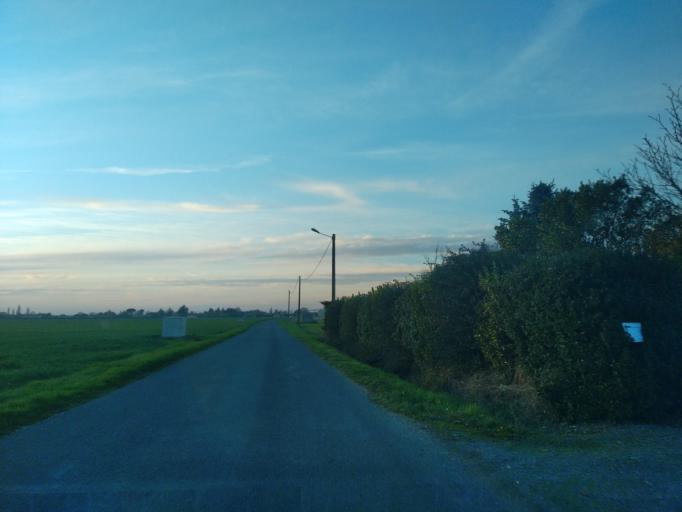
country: FR
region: Pays de la Loire
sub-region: Departement de la Vendee
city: Vix
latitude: 46.3969
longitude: -0.8330
